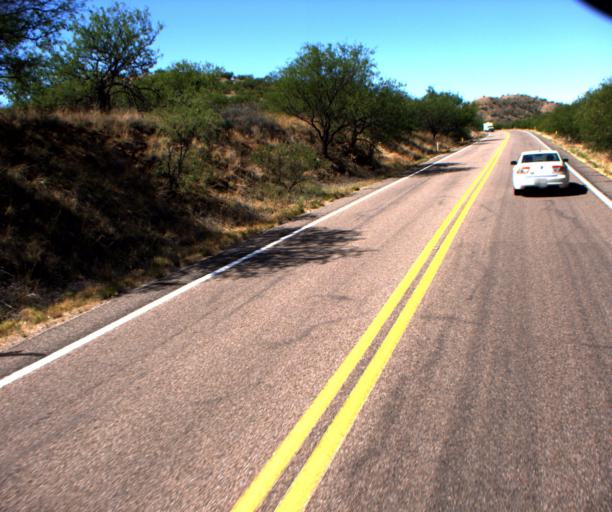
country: US
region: Arizona
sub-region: Santa Cruz County
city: Rio Rico
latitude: 31.4920
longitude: -110.8139
